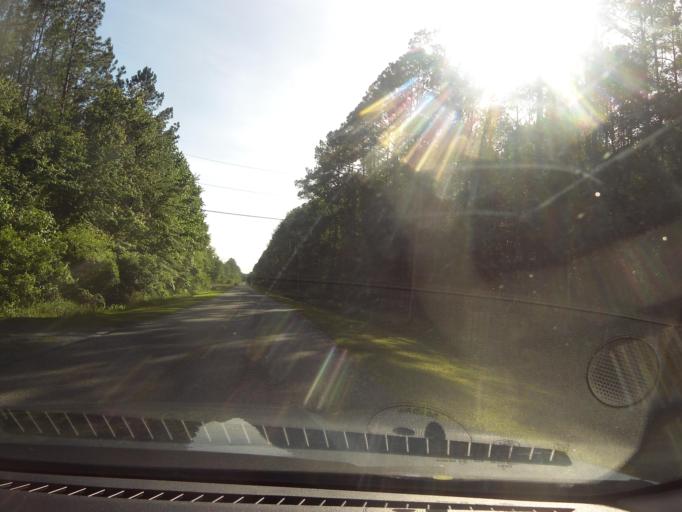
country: US
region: Florida
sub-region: Nassau County
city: Nassau Village-Ratliff
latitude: 30.4877
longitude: -81.8348
